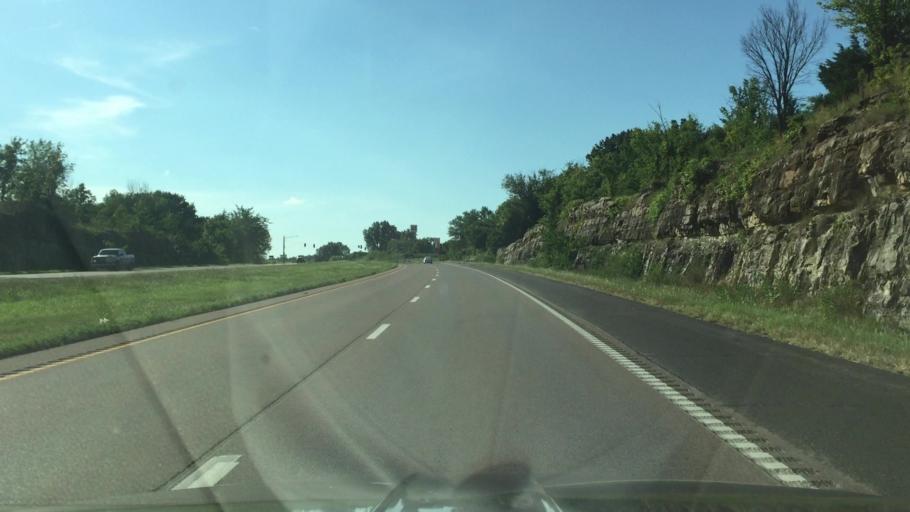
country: US
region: Missouri
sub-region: Pettis County
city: Sedalia
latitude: 38.7325
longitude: -93.3082
